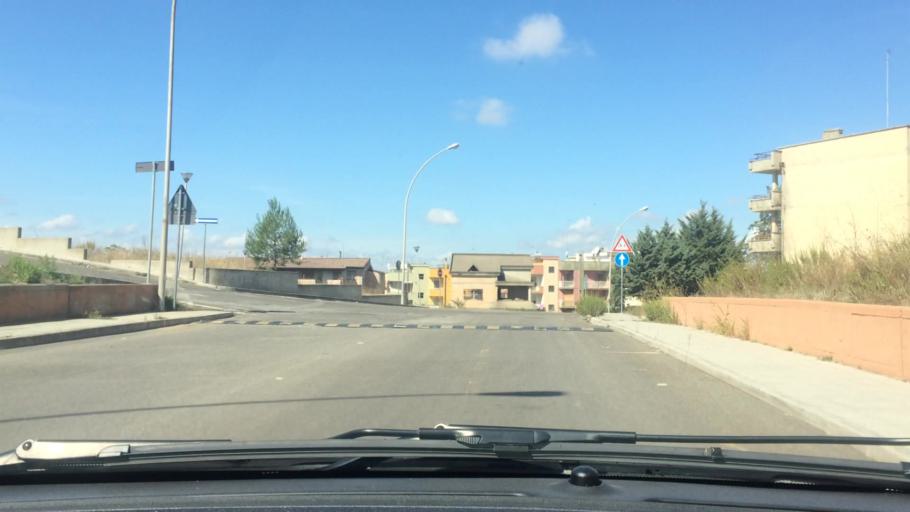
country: IT
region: Basilicate
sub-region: Provincia di Matera
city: Montescaglioso
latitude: 40.5447
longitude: 16.6680
